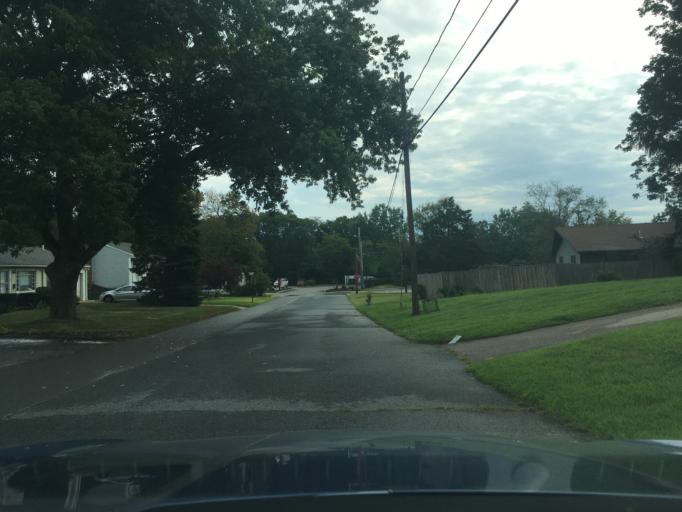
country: US
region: Rhode Island
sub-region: Kent County
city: East Greenwich
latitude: 41.6497
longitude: -71.4610
